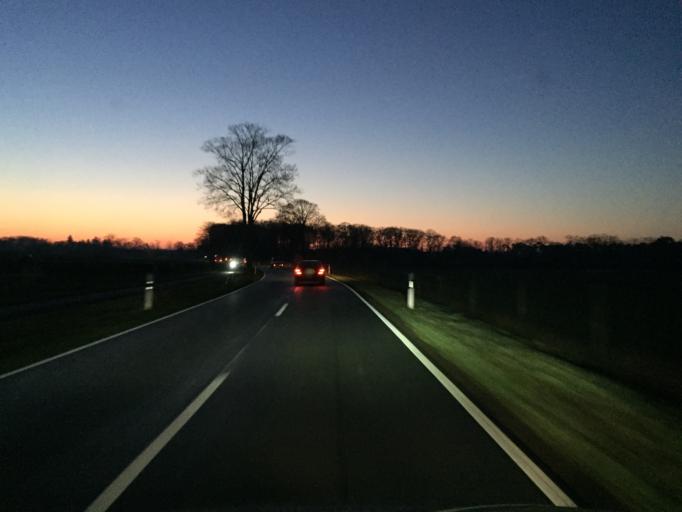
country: DE
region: Lower Saxony
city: Borstel
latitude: 52.6026
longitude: 8.9408
